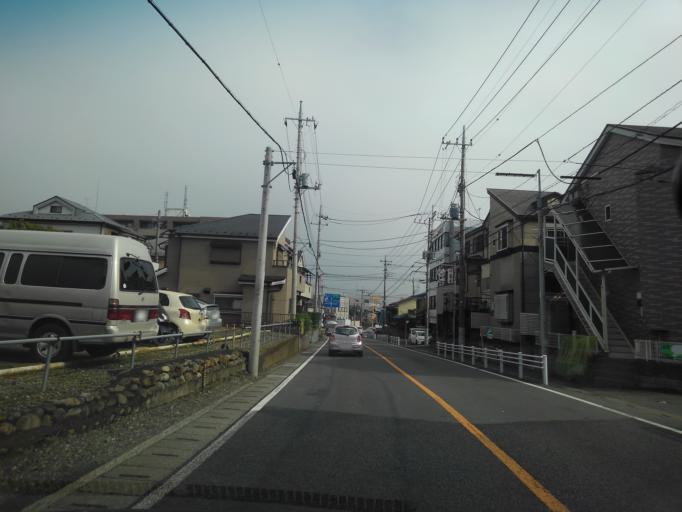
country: JP
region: Saitama
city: Tokorozawa
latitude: 35.7945
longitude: 139.4603
